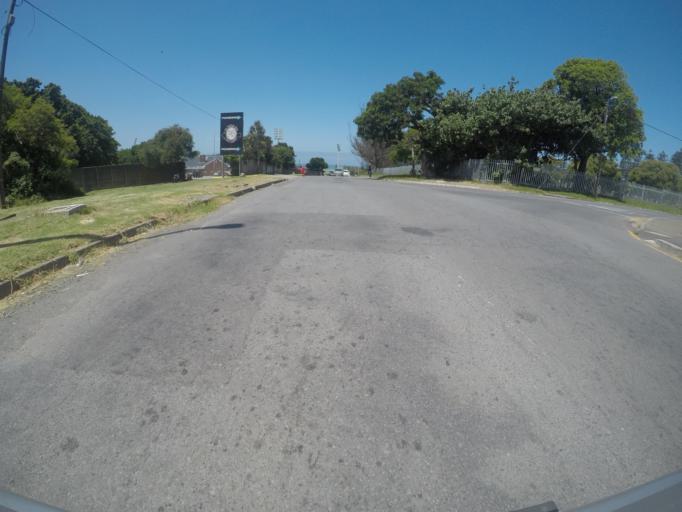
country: ZA
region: Eastern Cape
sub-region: Buffalo City Metropolitan Municipality
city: East London
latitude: -33.0074
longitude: 27.9160
